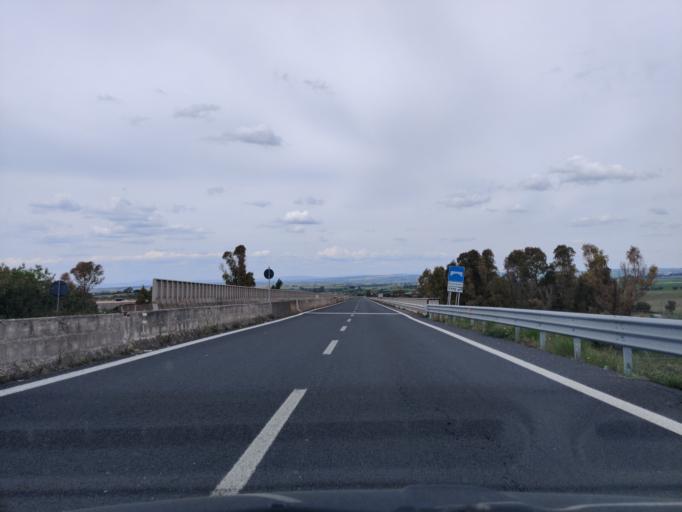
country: IT
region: Latium
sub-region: Citta metropolitana di Roma Capitale
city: Aurelia
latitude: 42.1387
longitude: 11.7946
